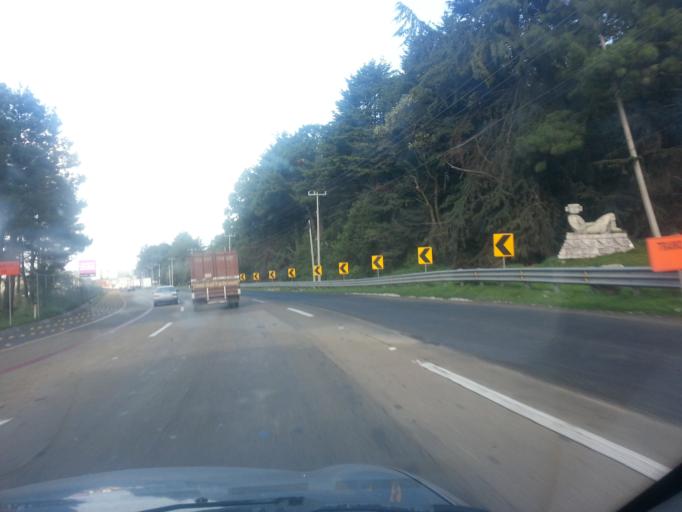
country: MX
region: Morelos
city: San Jeronimo Acazulco
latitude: 19.2966
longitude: -99.4179
